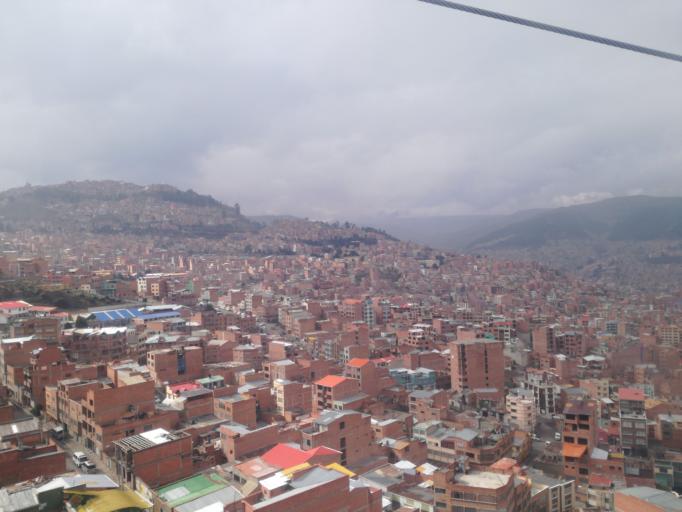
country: BO
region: La Paz
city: La Paz
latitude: -16.4980
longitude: -68.1588
